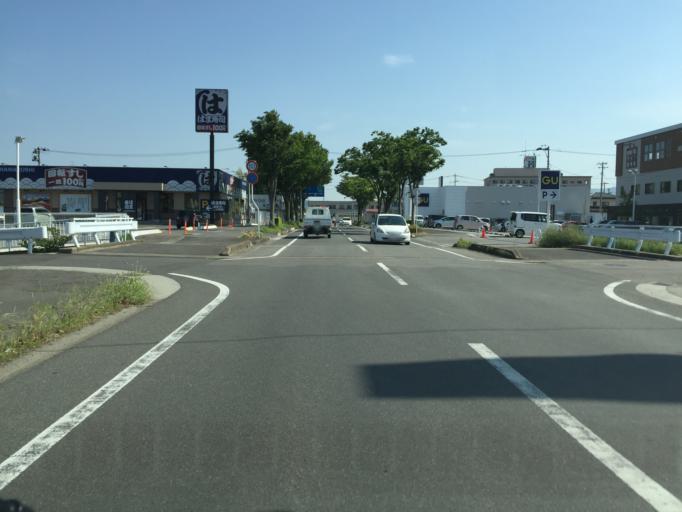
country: JP
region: Fukushima
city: Fukushima-shi
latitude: 37.7419
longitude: 140.4456
